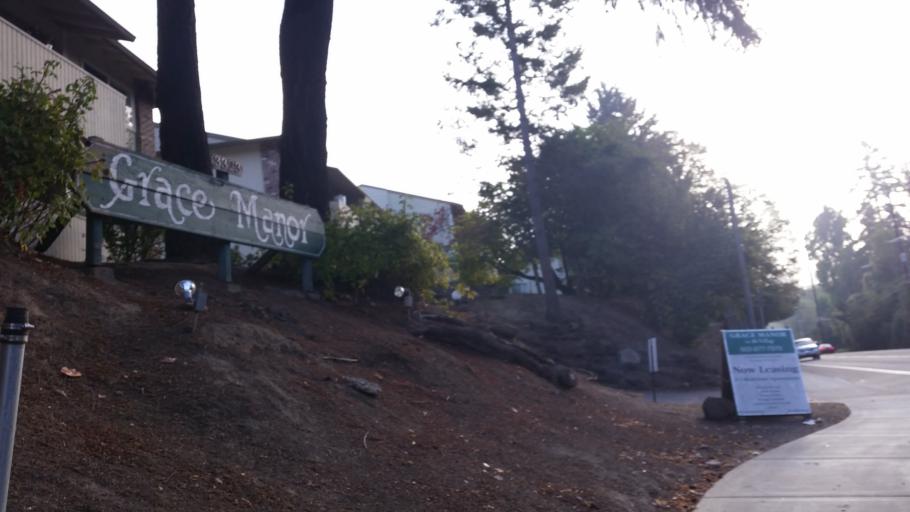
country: US
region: Oregon
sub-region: Washington County
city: Garden Home-Whitford
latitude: 45.4669
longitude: -122.7110
